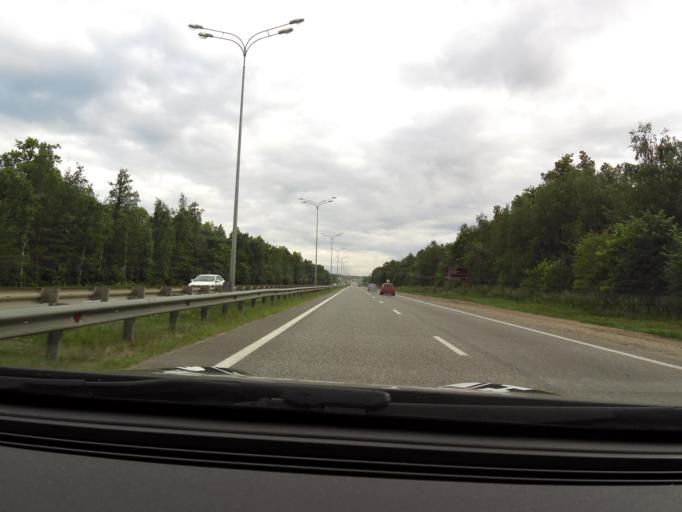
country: RU
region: Tatarstan
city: Sviyazhsk
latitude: 55.7477
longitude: 48.7969
